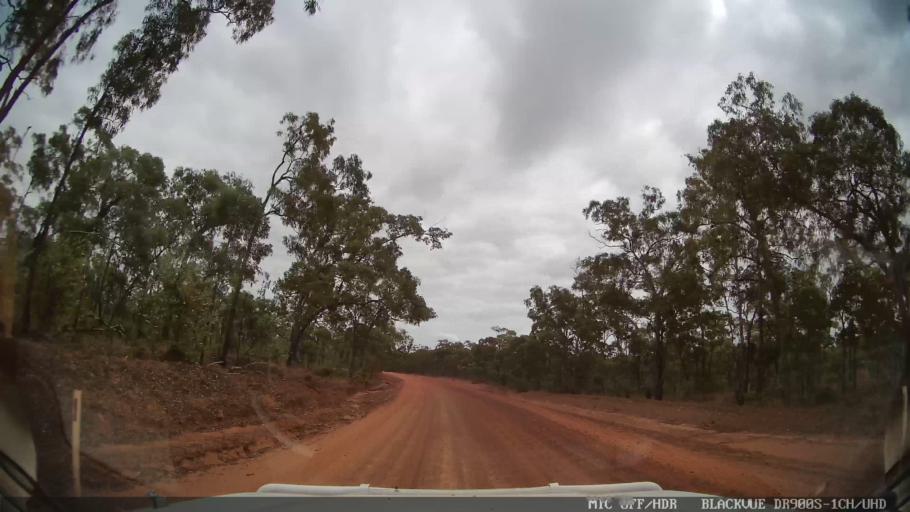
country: AU
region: Queensland
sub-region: Cook
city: Cooktown
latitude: -15.2639
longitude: 144.9551
